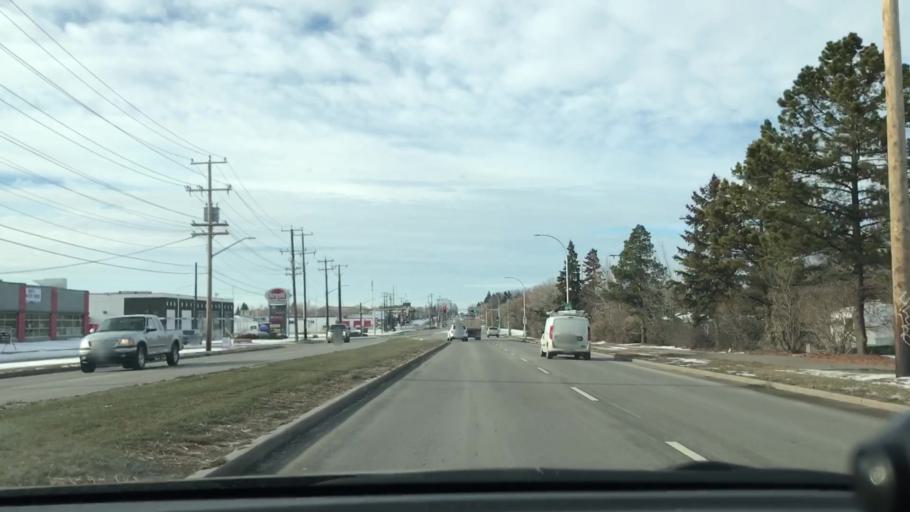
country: CA
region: Alberta
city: Edmonton
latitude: 53.5000
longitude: -113.4640
